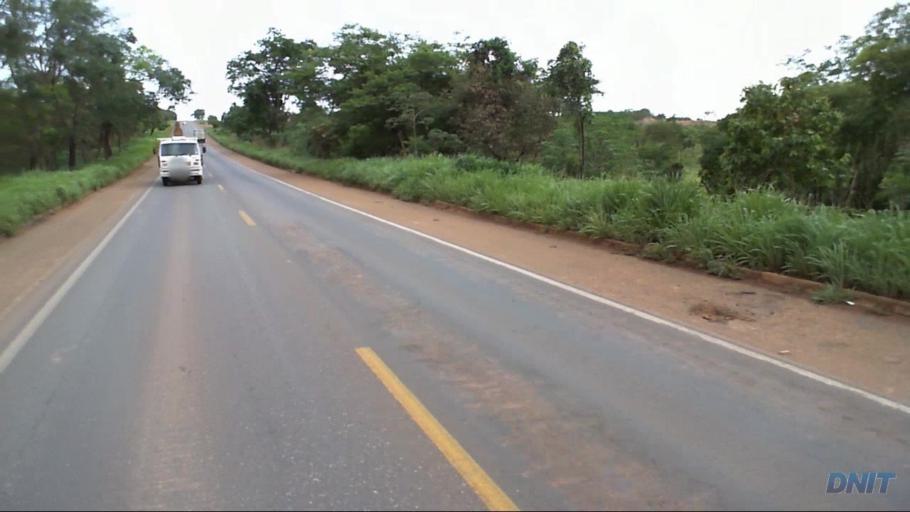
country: BR
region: Goias
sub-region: Uruacu
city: Uruacu
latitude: -14.5515
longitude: -49.1595
